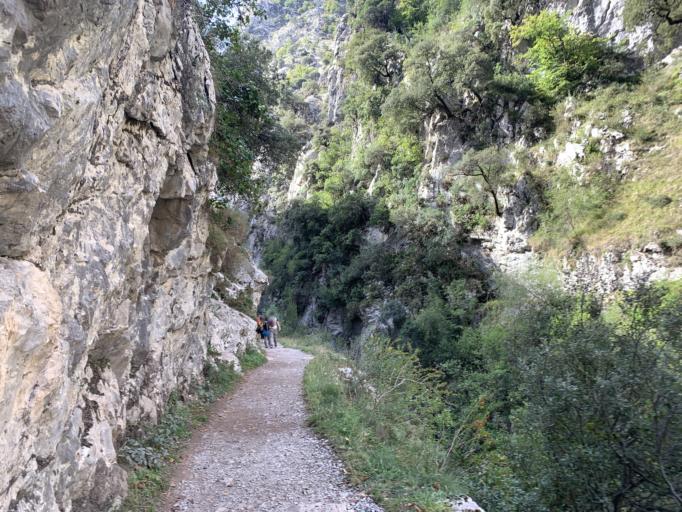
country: ES
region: Castille and Leon
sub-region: Provincia de Leon
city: Posada de Valdeon
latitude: 43.2270
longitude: -4.8950
